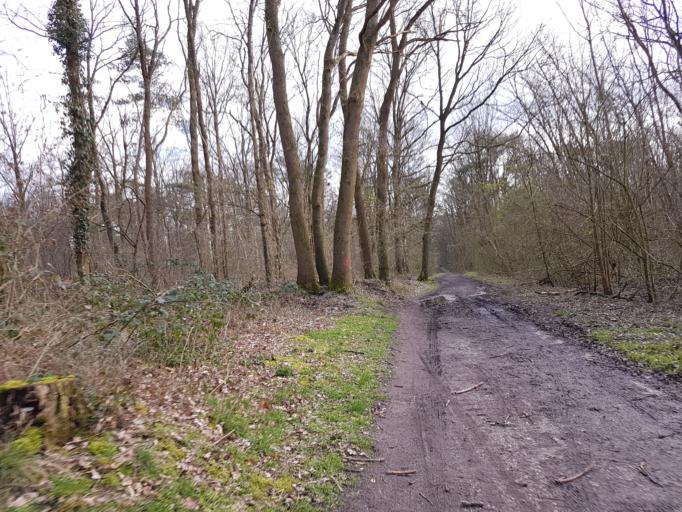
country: DE
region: North Rhine-Westphalia
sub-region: Regierungsbezirk Dusseldorf
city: Bruggen
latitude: 51.2496
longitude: 6.1951
